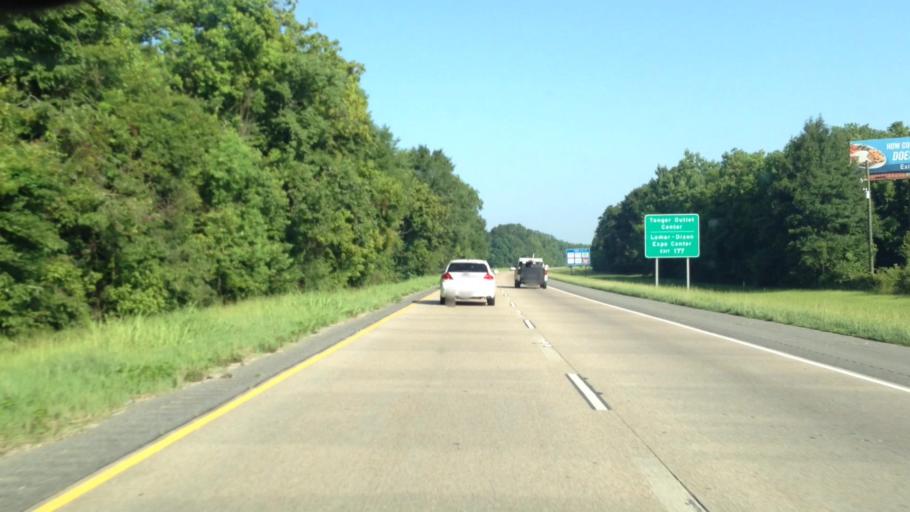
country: US
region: Louisiana
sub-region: Ascension Parish
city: Gonzales
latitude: 30.1988
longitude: -90.9328
